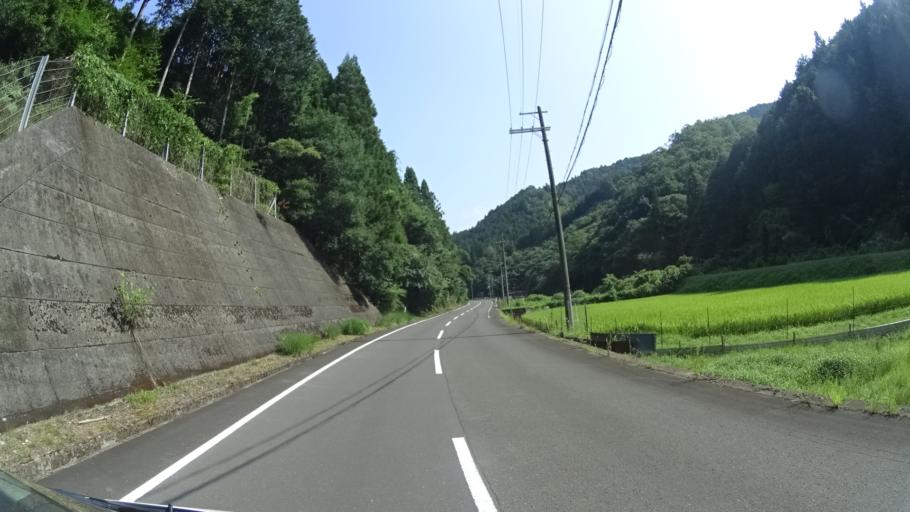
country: JP
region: Kyoto
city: Maizuru
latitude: 35.4196
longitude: 135.2258
